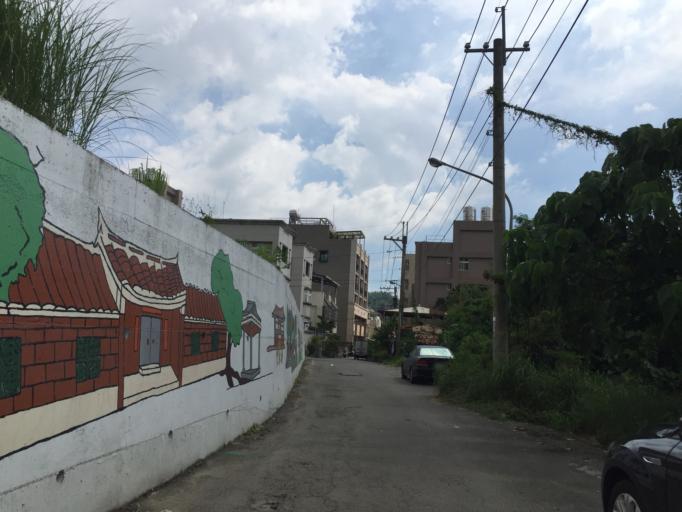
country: TW
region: Taiwan
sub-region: Taichung City
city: Taichung
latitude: 24.0748
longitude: 120.7170
